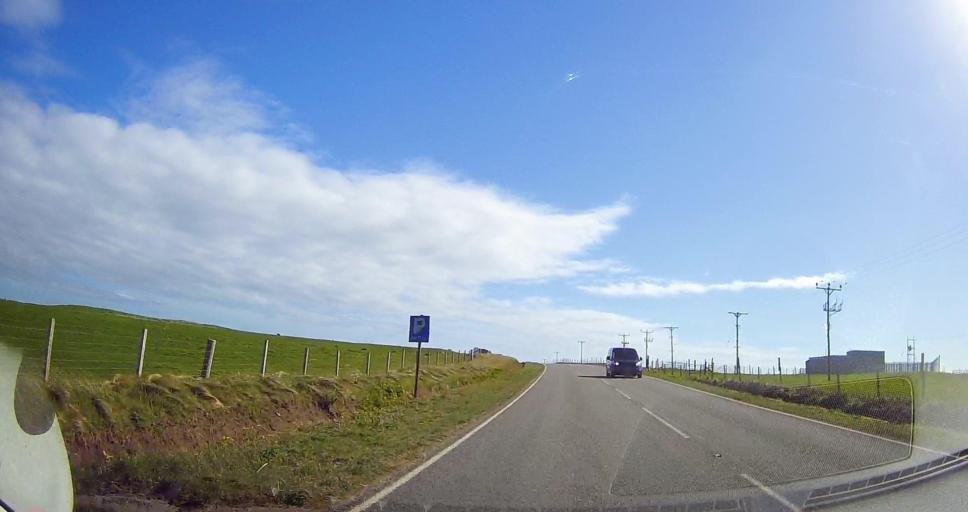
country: GB
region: Scotland
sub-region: Shetland Islands
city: Sandwick
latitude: 59.8995
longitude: -1.3034
